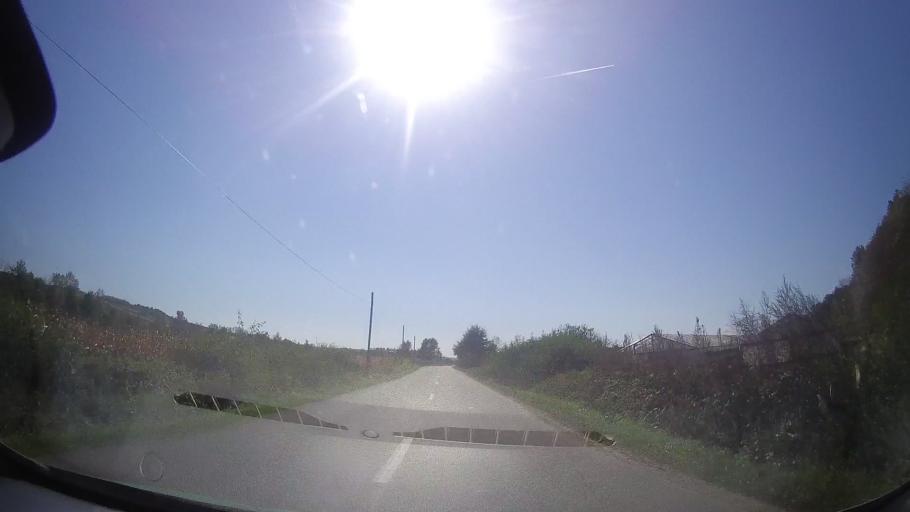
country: RO
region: Timis
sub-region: Comuna Ohaba Lunga
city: Ohaba Lunga
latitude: 45.8807
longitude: 21.9643
